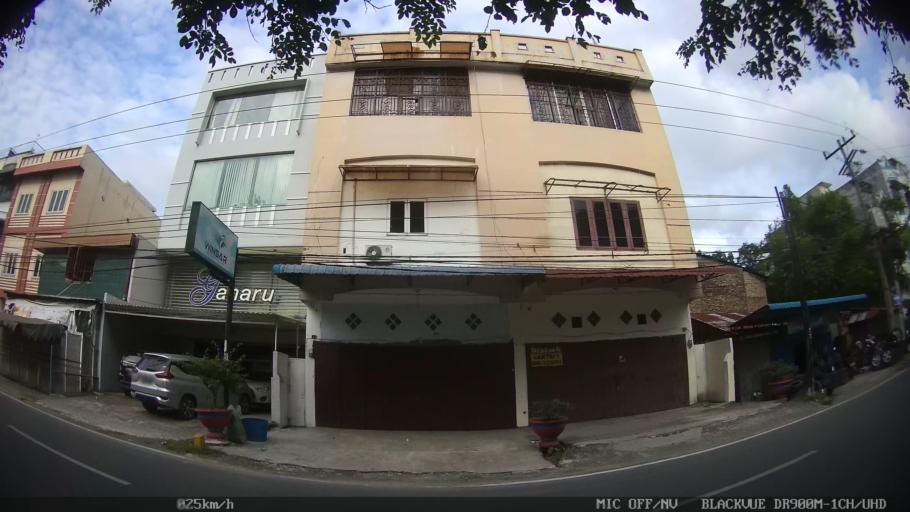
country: ID
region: North Sumatra
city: Medan
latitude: 3.6026
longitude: 98.6769
